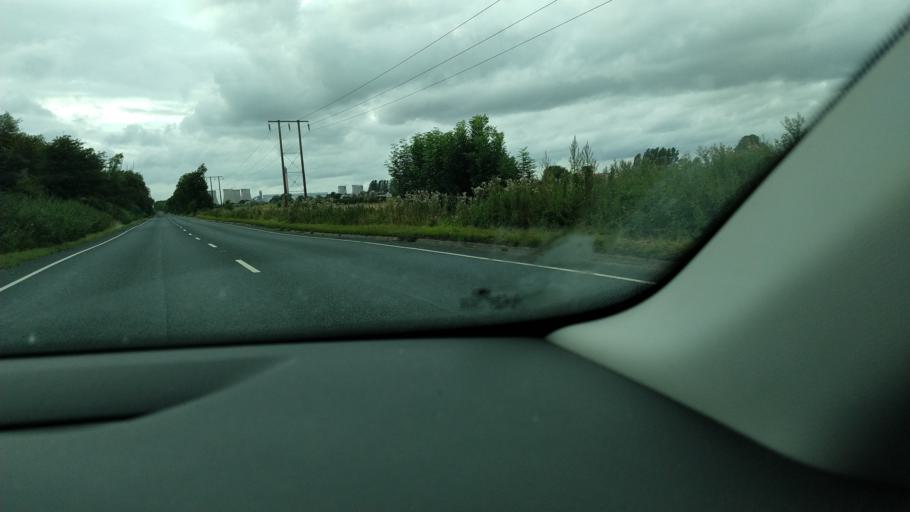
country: GB
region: England
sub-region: East Riding of Yorkshire
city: Rawcliffe
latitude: 53.7090
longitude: -0.9431
